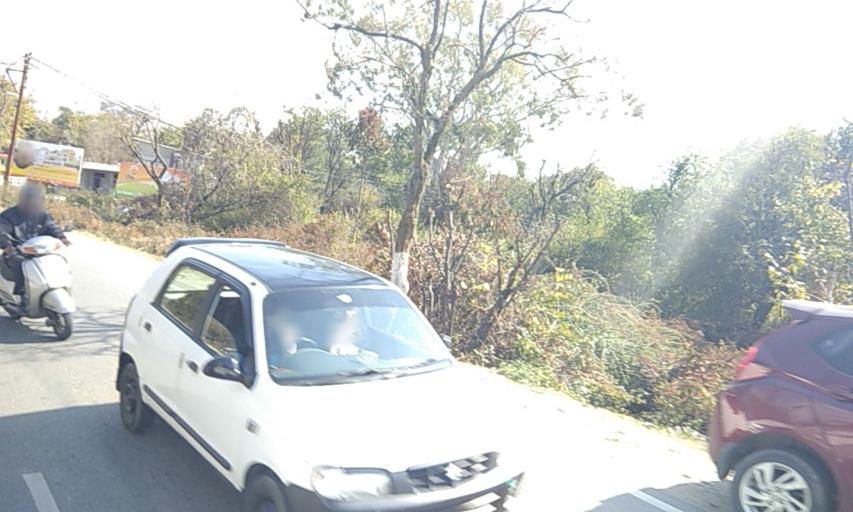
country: IN
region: Himachal Pradesh
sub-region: Kangra
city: Dharmsala
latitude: 32.1867
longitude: 76.3622
